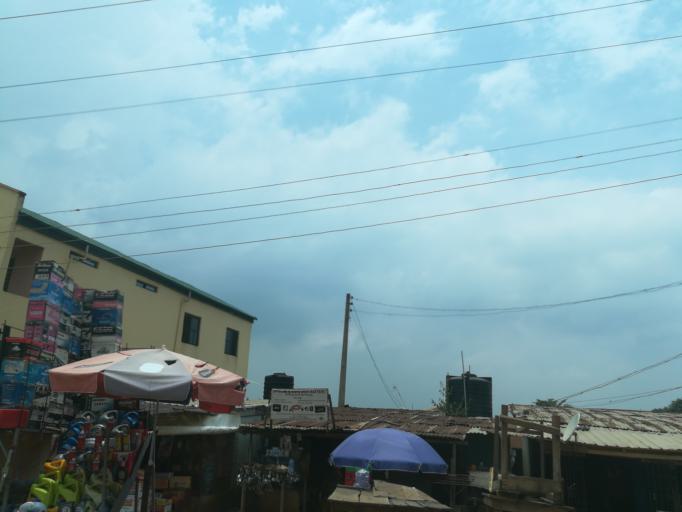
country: NG
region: Lagos
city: Ikorodu
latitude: 6.6255
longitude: 3.5524
